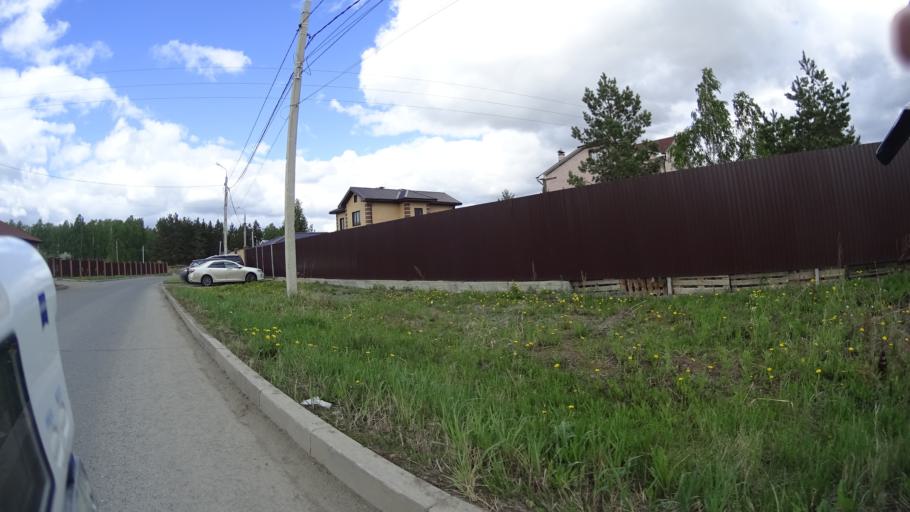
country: RU
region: Chelyabinsk
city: Sargazy
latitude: 55.1609
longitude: 61.2519
